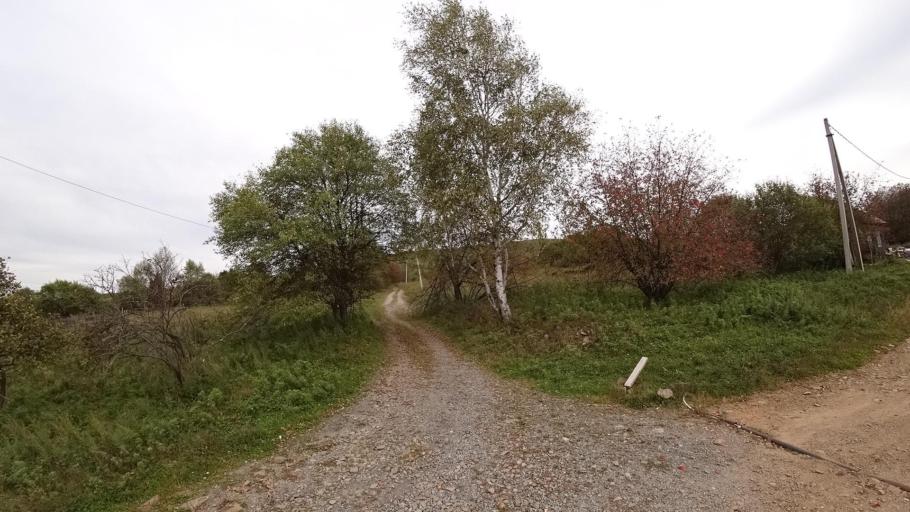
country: RU
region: Jewish Autonomous Oblast
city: Khingansk
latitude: 49.1289
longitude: 131.2023
